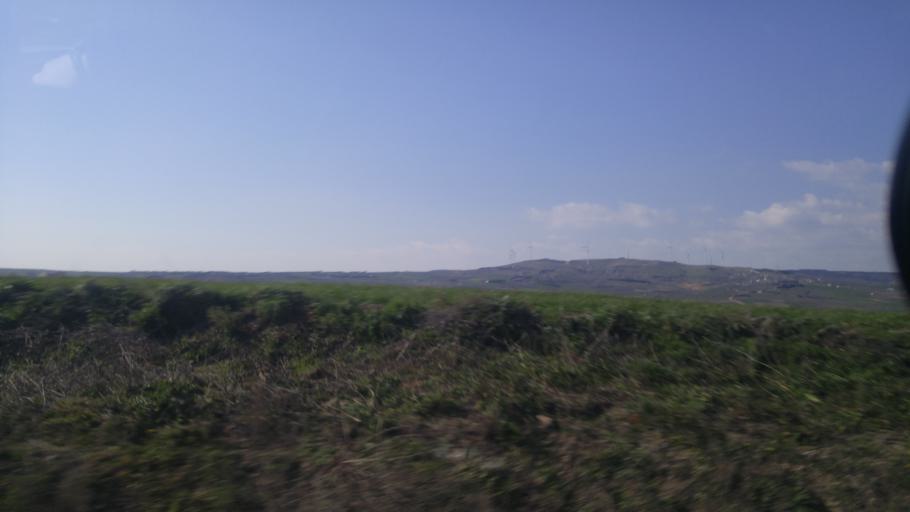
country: TR
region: Istanbul
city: Canta
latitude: 41.1007
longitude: 28.1108
